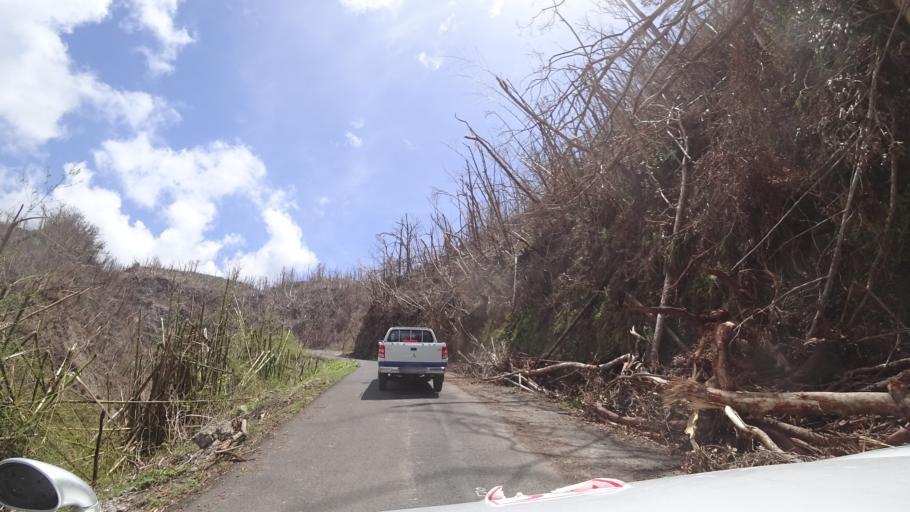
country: DM
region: Saint Luke
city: Pointe Michel
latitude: 15.2704
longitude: -61.3514
